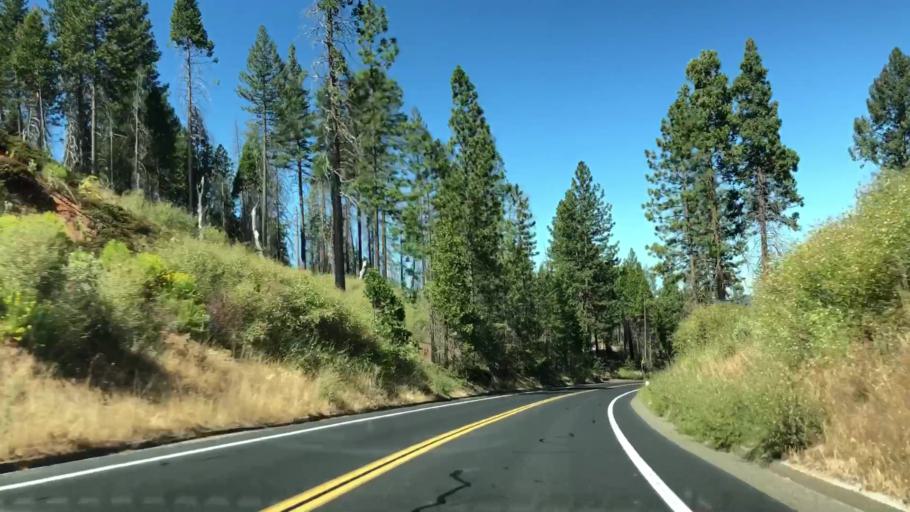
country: US
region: California
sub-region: Mariposa County
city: Midpines
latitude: 37.8278
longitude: -119.9793
